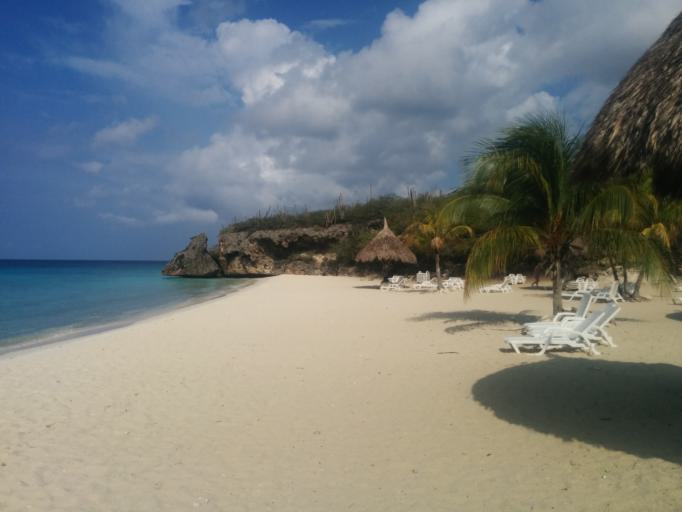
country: CW
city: Dorp Soto
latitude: 12.2283
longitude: -69.0924
